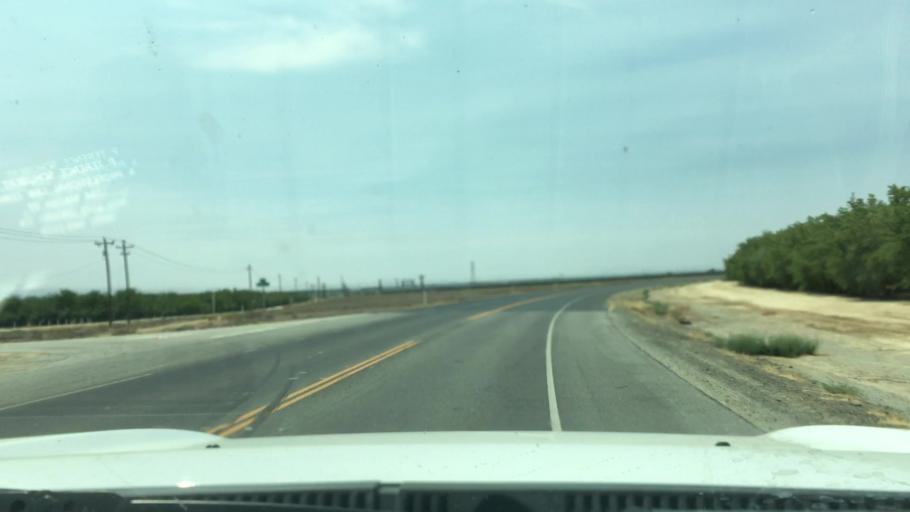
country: US
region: California
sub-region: Kern County
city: Lost Hills
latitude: 35.6014
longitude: -119.5712
